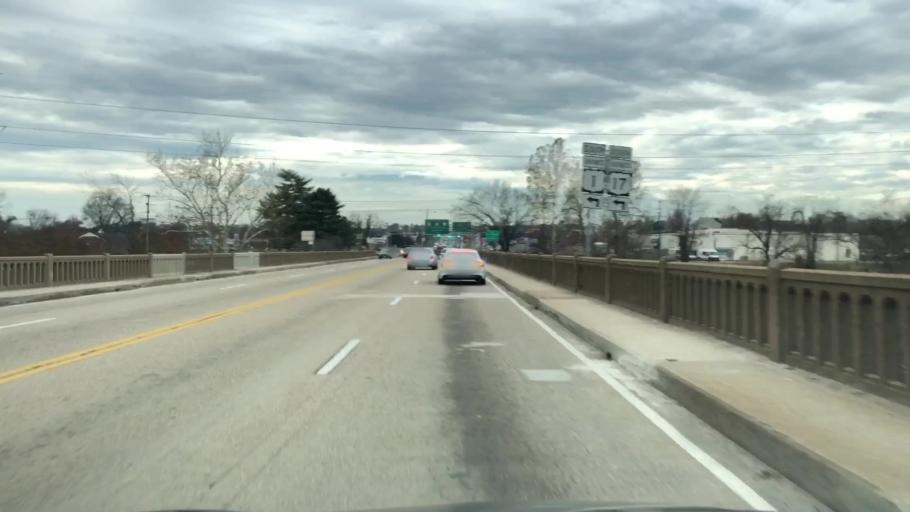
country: US
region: Virginia
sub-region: Stafford County
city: Falmouth
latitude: 38.3201
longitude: -77.4710
